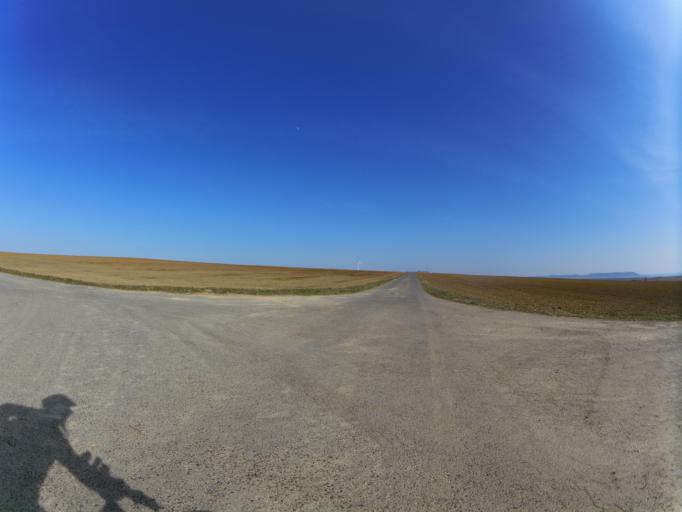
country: DE
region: Bavaria
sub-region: Regierungsbezirk Unterfranken
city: Prosselsheim
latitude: 49.8313
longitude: 10.1204
